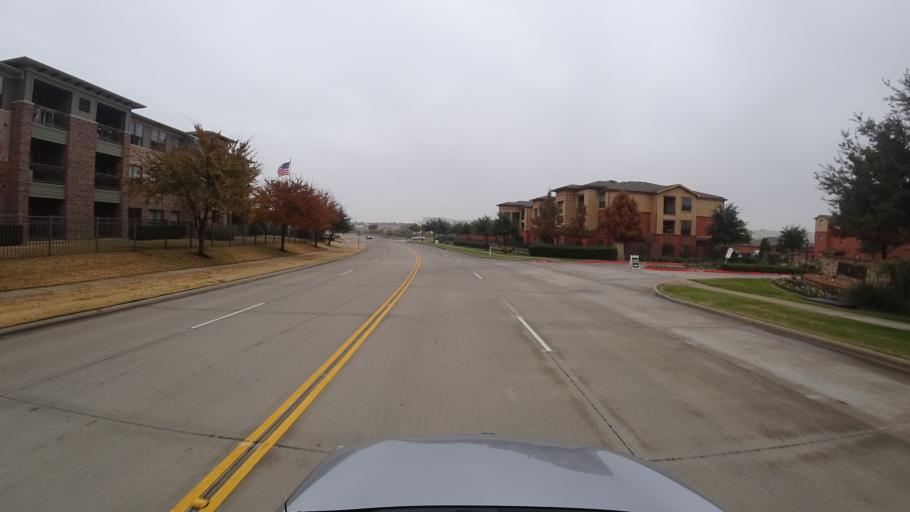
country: US
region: Texas
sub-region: Denton County
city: The Colony
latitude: 33.0606
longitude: -96.9139
